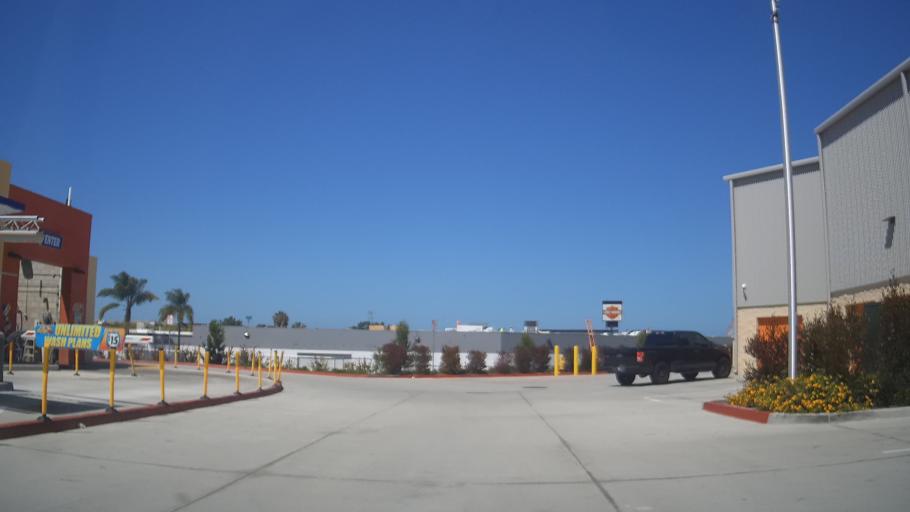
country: US
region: California
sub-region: San Diego County
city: Chula Vista
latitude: 32.6546
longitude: -117.0992
